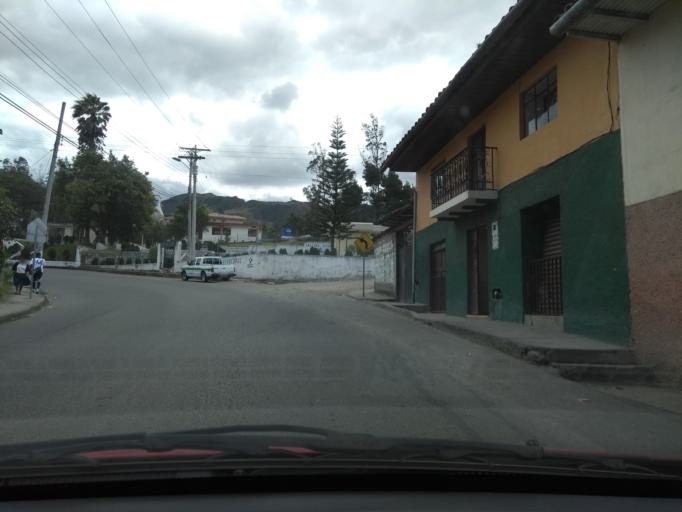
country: EC
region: Azuay
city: Cuenca
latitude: -3.1581
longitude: -79.1509
